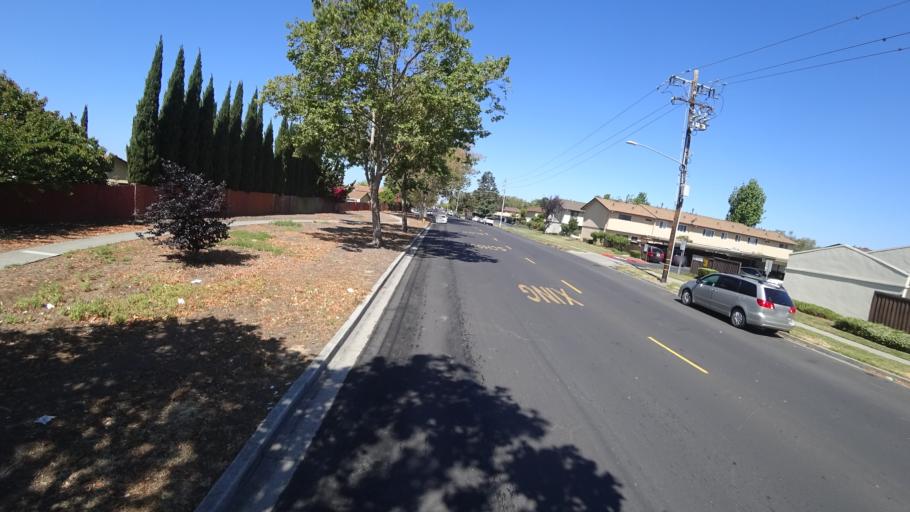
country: US
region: California
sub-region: Alameda County
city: Hayward
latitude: 37.6241
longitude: -122.0948
